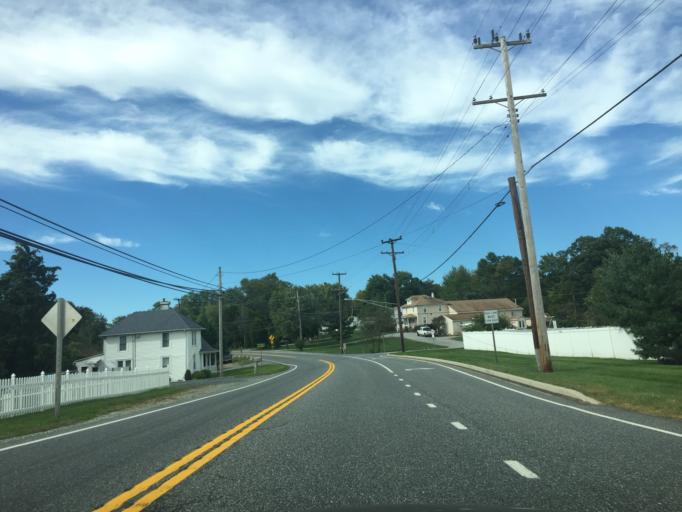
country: US
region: Maryland
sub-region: Harford County
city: Joppatowne
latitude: 39.4331
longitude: -76.3606
